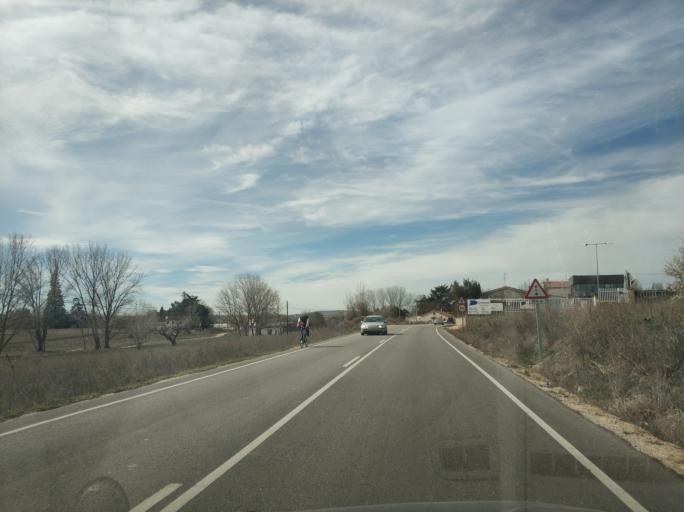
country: ES
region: Castille and Leon
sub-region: Provincia de Salamanca
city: Cabrerizos
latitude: 40.9726
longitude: -5.6200
